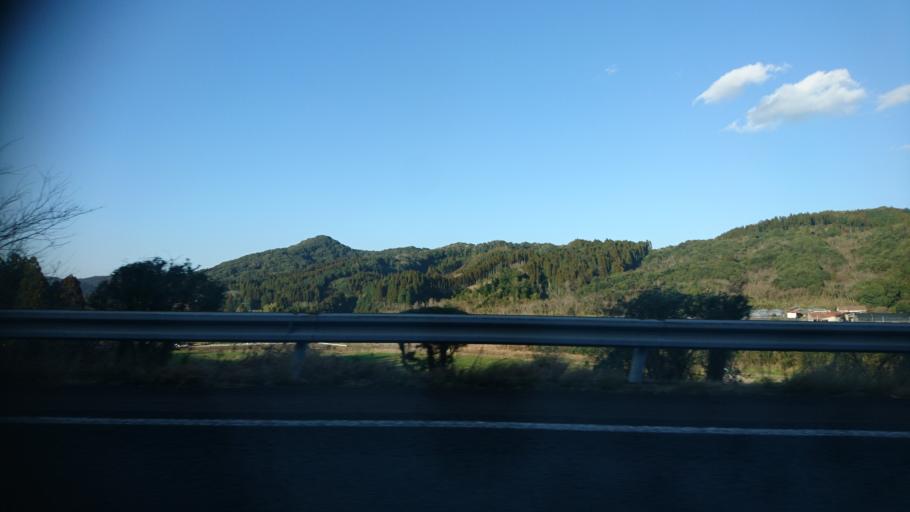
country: JP
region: Miyazaki
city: Miyakonojo
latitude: 31.7945
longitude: 131.1749
